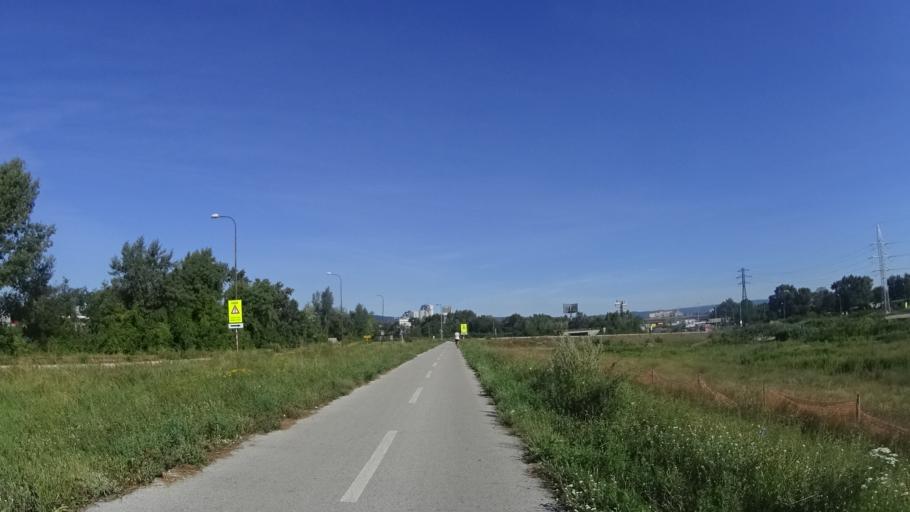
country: SK
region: Bratislavsky
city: Bratislava
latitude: 48.1361
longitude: 17.1529
